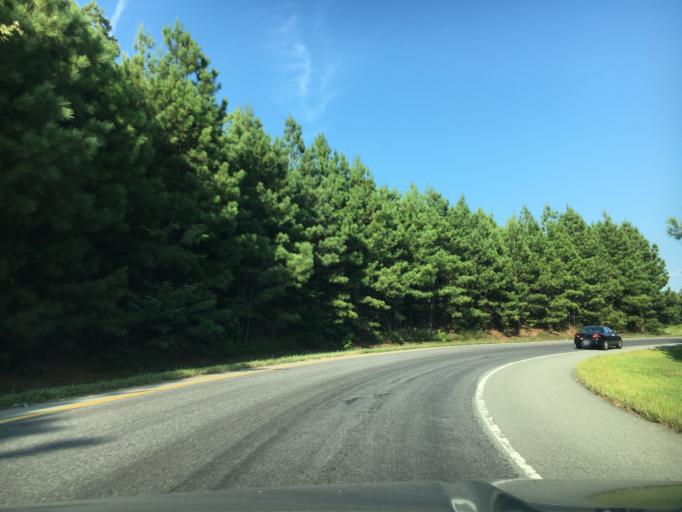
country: US
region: Virginia
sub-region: Henrico County
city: Short Pump
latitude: 37.6019
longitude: -77.6679
